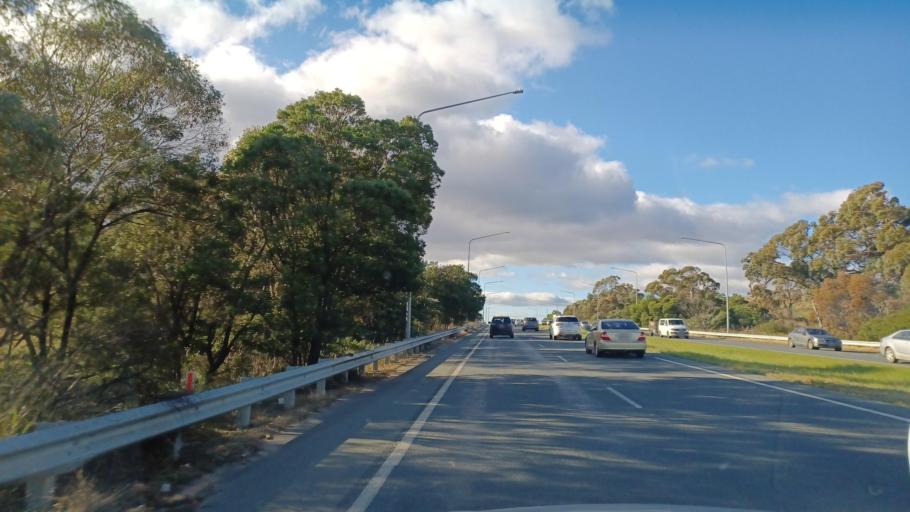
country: AU
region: Australian Capital Territory
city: Macquarie
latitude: -35.2723
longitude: 149.0585
